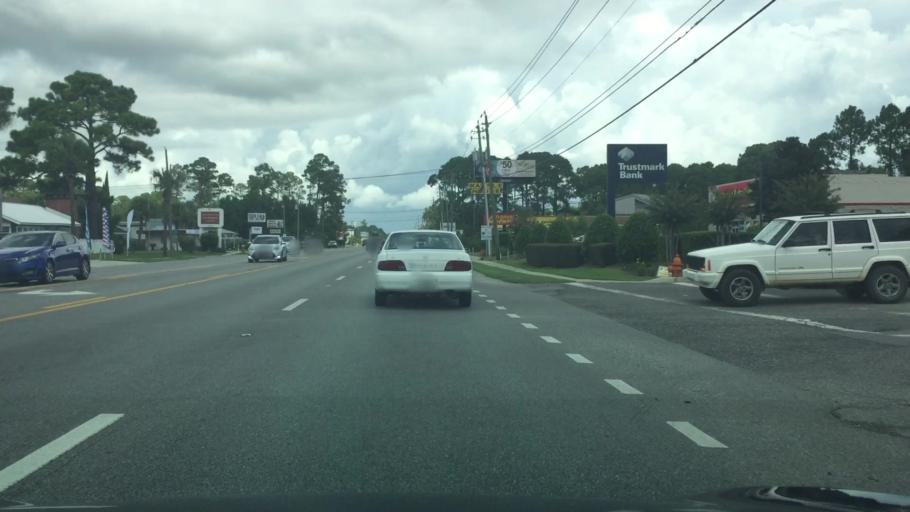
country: US
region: Florida
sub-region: Bay County
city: Upper Grand Lagoon
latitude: 30.1613
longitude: -85.7542
